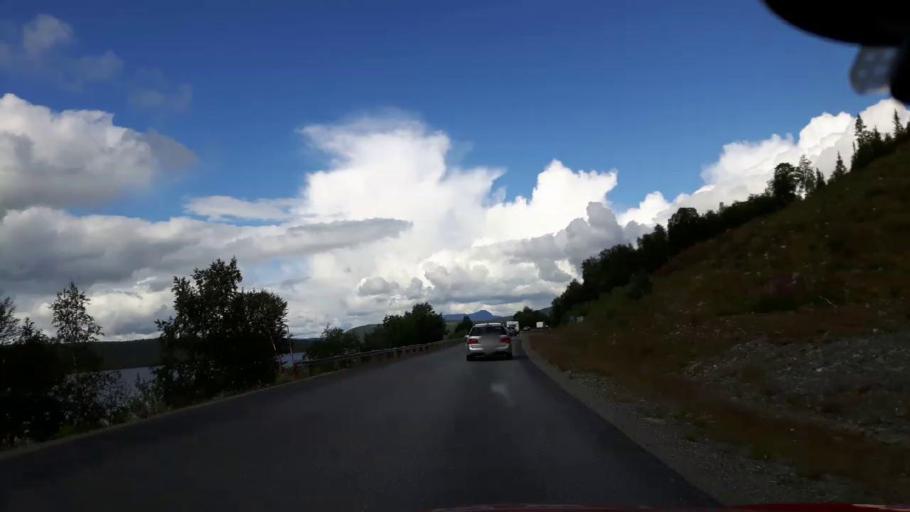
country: SE
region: Vaesterbotten
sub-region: Vilhelmina Kommun
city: Sjoberg
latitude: 65.0391
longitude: 15.1168
